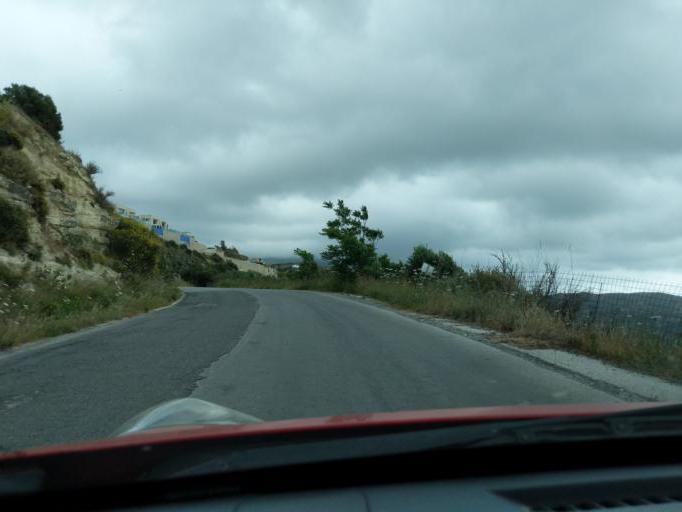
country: GR
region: Crete
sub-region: Nomos Chanias
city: Platanos
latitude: 35.4815
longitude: 23.5917
